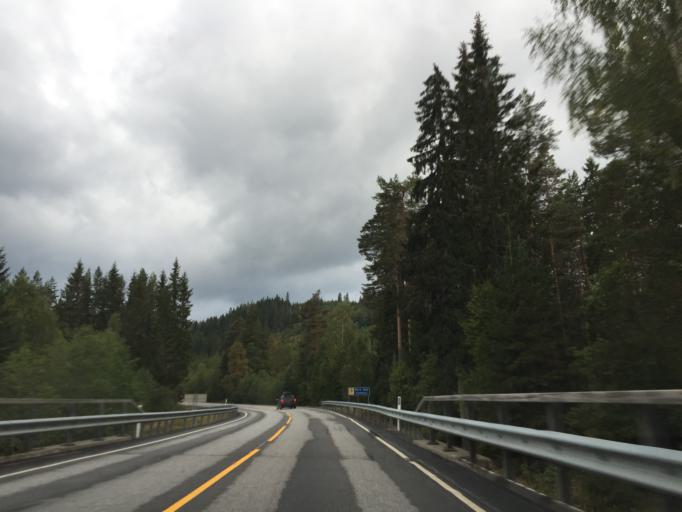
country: NO
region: Hedmark
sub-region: Nord-Odal
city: Sand
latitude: 60.5168
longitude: 11.5104
